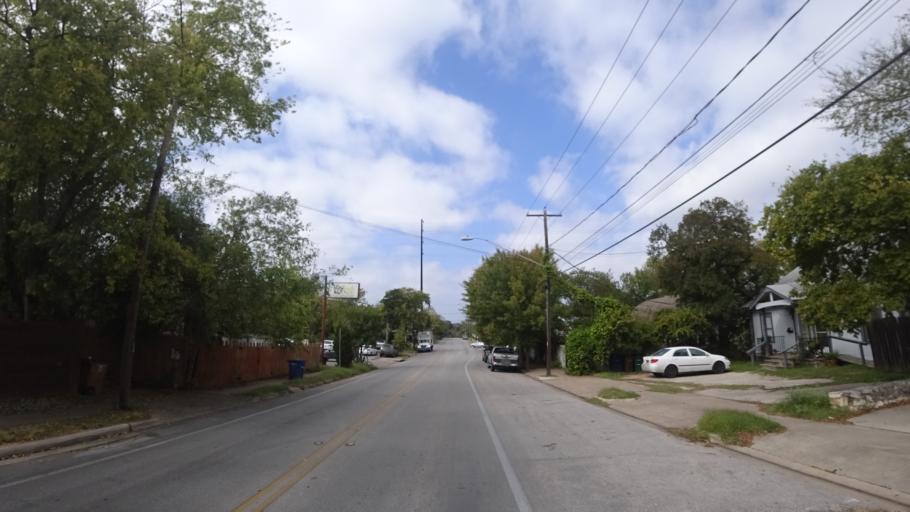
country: US
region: Texas
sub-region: Travis County
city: Austin
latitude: 30.2480
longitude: -97.7611
